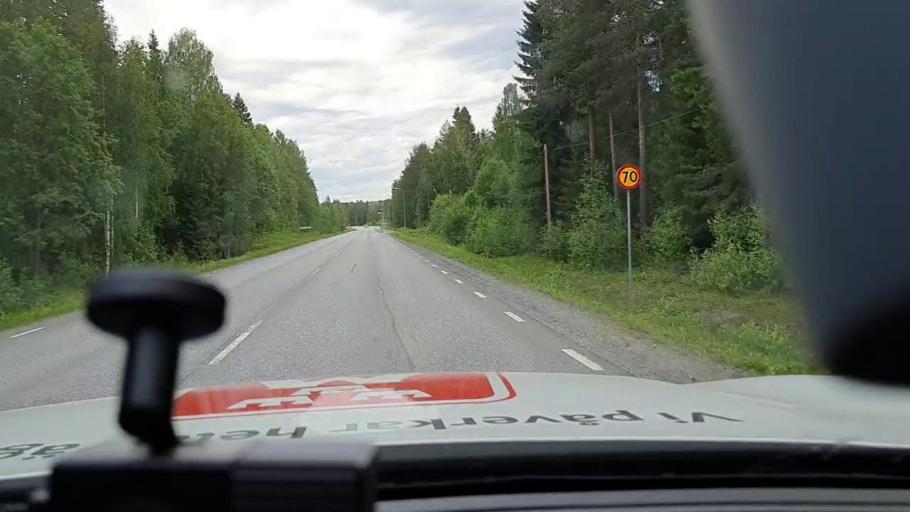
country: SE
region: Norrbotten
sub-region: Bodens Kommun
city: Boden
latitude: 65.8104
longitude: 21.6524
